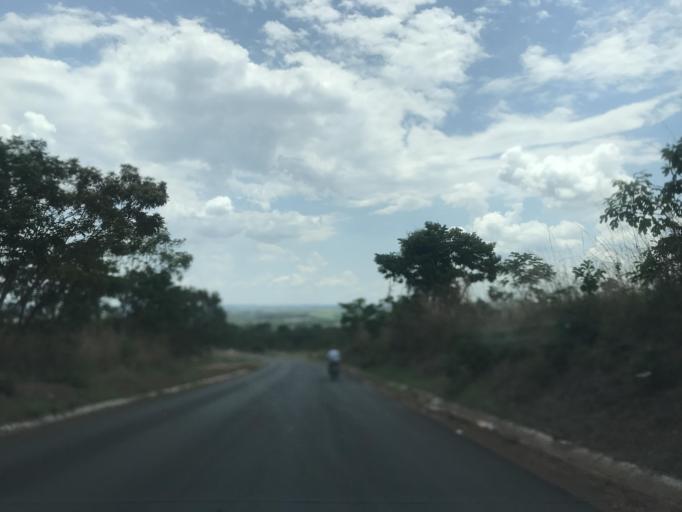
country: BR
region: Goias
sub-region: Bela Vista De Goias
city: Bela Vista de Goias
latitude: -17.0355
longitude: -48.6588
